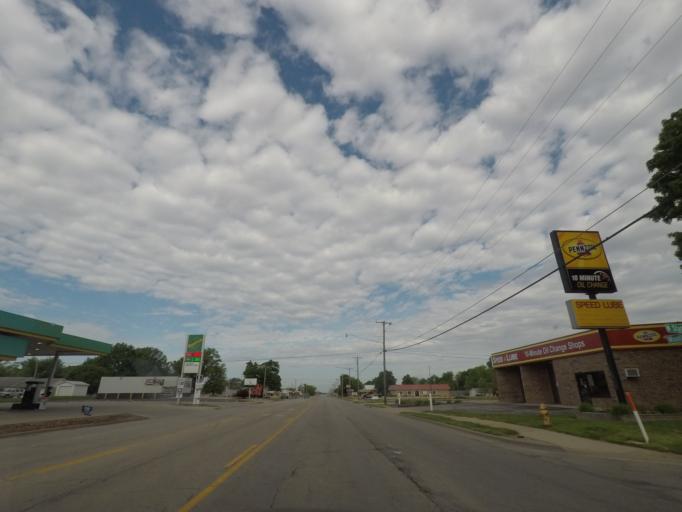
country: US
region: Illinois
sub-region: Logan County
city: Lincoln
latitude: 40.1577
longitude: -89.3774
